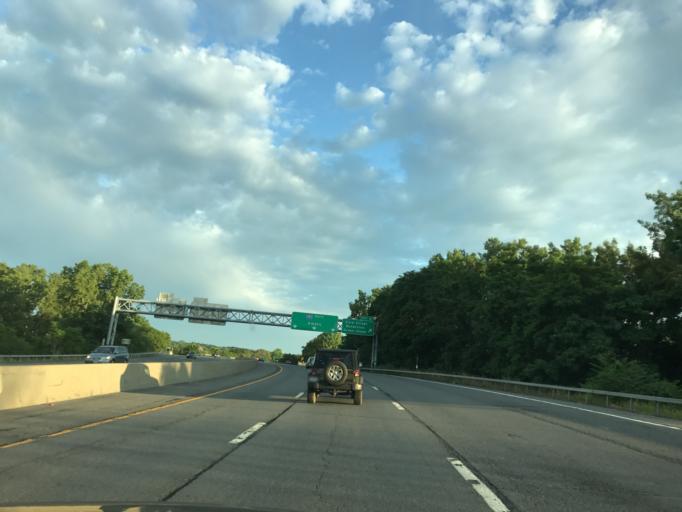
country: US
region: New York
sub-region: Albany County
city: Watervliet
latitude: 42.7373
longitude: -73.6993
